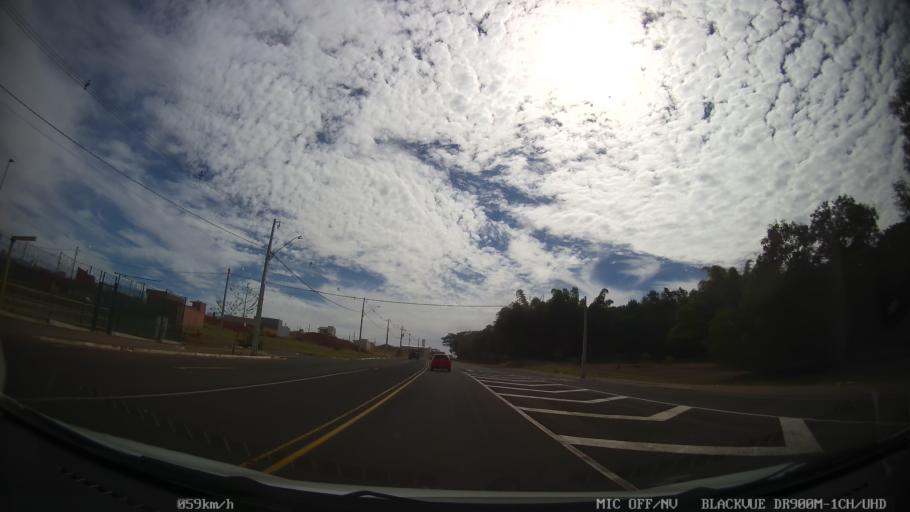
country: BR
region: Sao Paulo
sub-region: Catanduva
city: Catanduva
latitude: -21.1694
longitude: -48.9621
